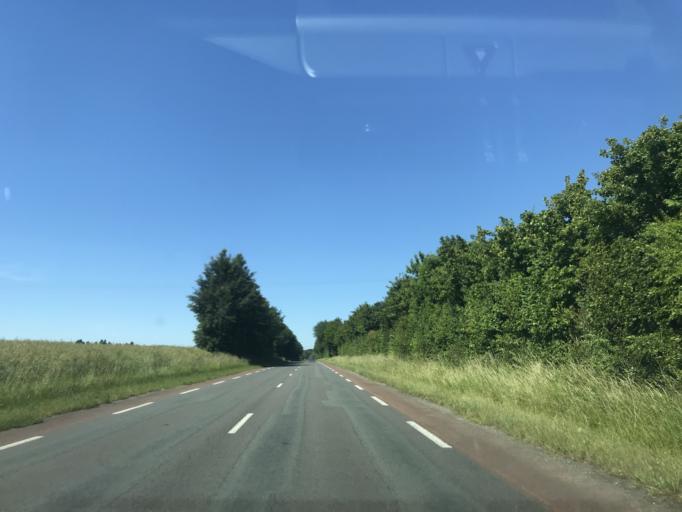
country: FR
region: Poitou-Charentes
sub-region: Departement de la Charente-Maritime
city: Gemozac
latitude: 45.5744
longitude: -0.6919
